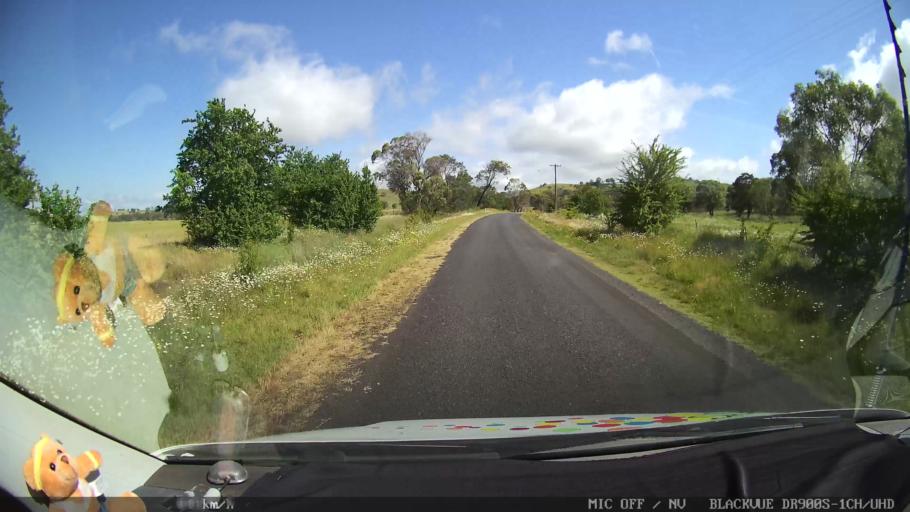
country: AU
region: New South Wales
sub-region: Guyra
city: Guyra
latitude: -30.0154
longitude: 151.6578
